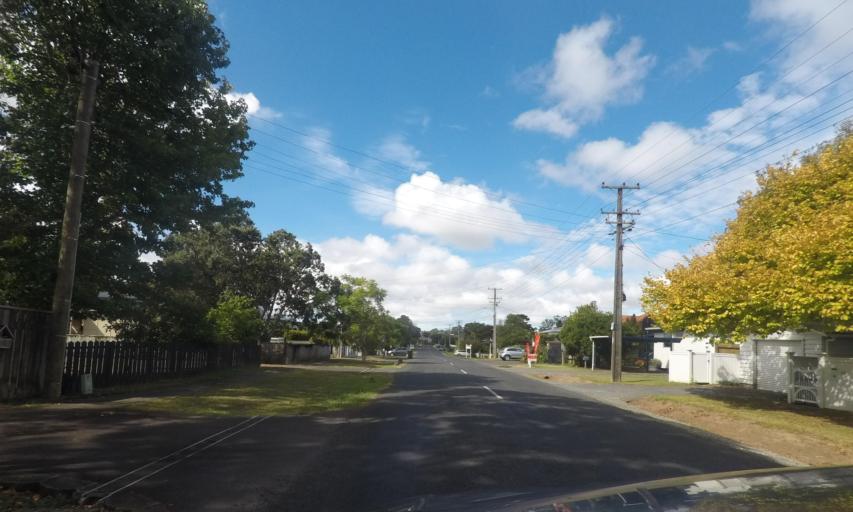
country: NZ
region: Auckland
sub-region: Auckland
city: Rosebank
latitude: -36.7803
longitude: 174.6561
